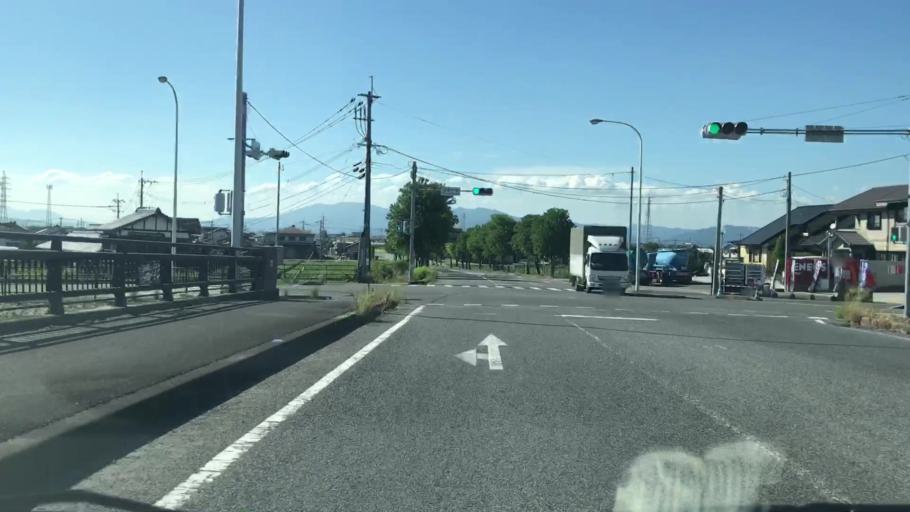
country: JP
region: Saga Prefecture
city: Okawa
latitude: 33.2285
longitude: 130.3699
